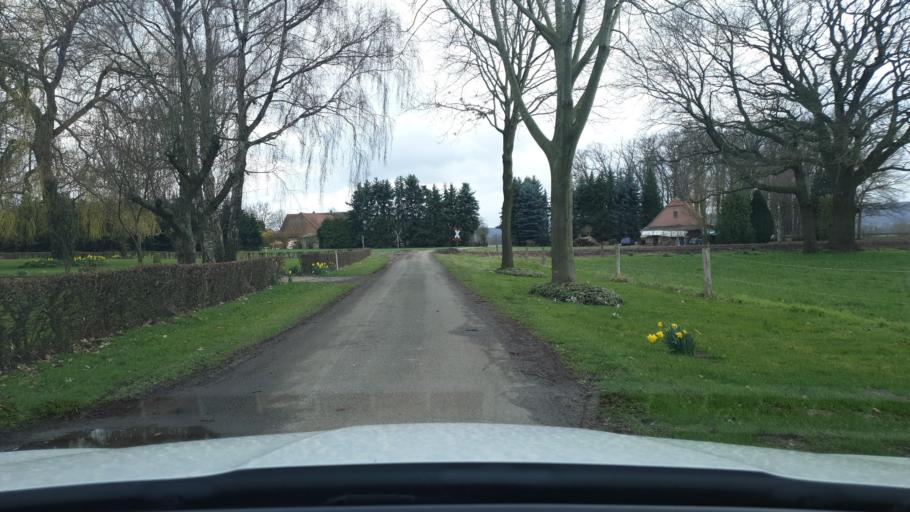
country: DE
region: North Rhine-Westphalia
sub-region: Regierungsbezirk Detmold
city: Hille
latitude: 52.3290
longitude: 8.7733
